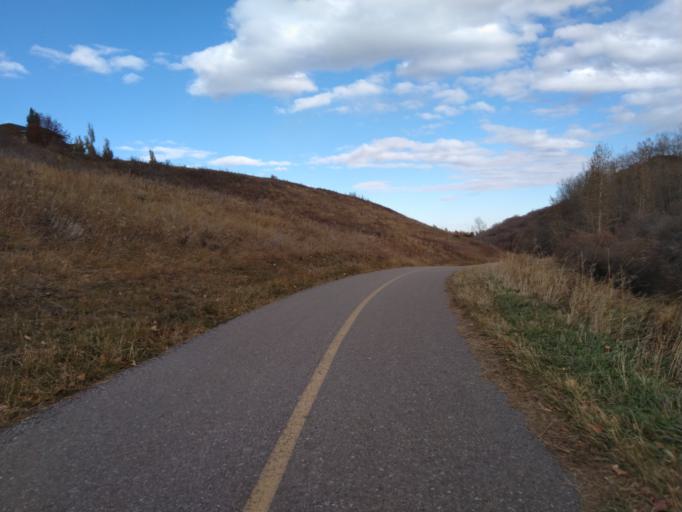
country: CA
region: Alberta
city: Calgary
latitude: 51.1372
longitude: -114.1365
